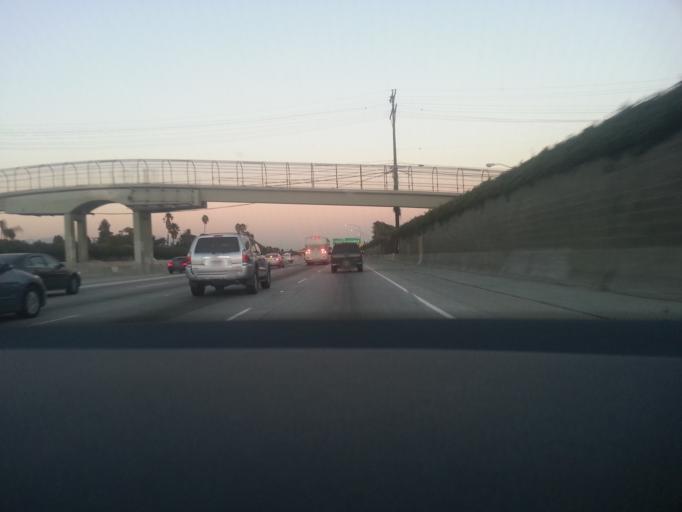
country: US
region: California
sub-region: Los Angeles County
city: Monterey Park
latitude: 34.0713
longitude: -118.1389
